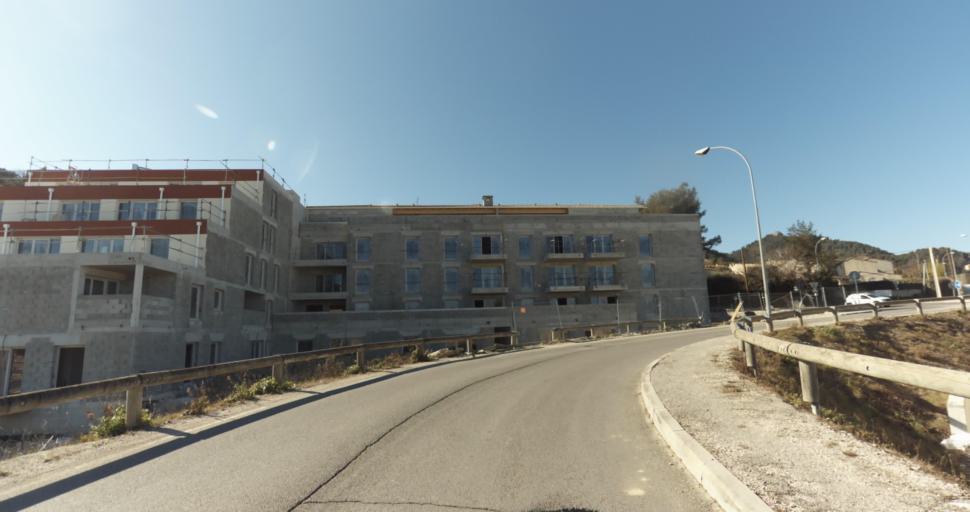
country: FR
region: Provence-Alpes-Cote d'Azur
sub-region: Departement des Bouches-du-Rhone
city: Cadolive
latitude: 43.3908
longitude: 5.5515
